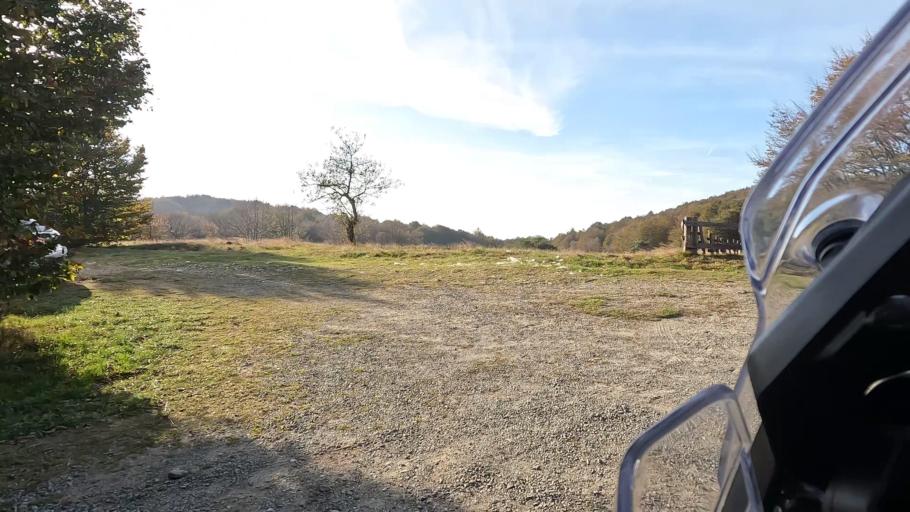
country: IT
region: Liguria
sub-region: Provincia di Savona
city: Urbe
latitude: 44.4321
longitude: 8.5593
